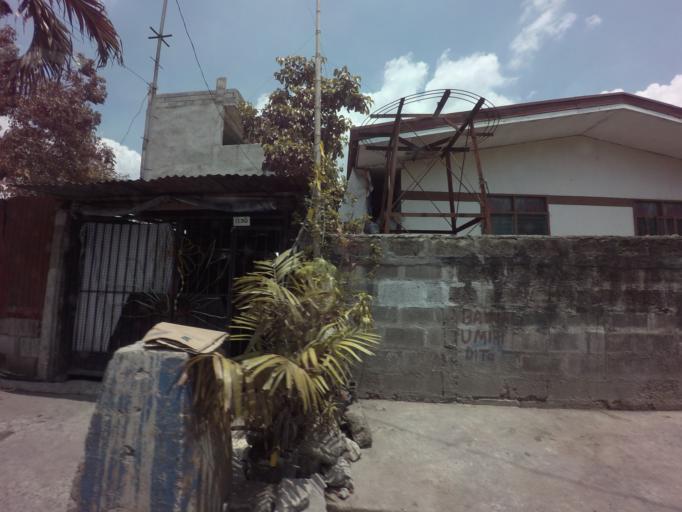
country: PH
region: Calabarzon
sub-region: Province of Laguna
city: San Pedro
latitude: 14.3890
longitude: 121.0499
